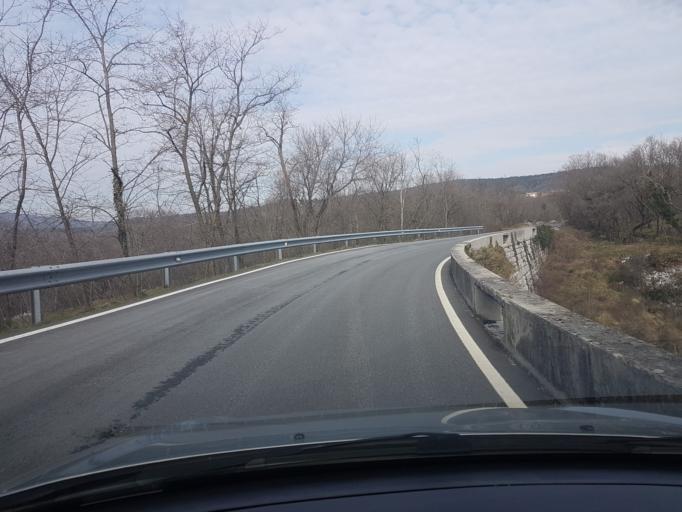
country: IT
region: Friuli Venezia Giulia
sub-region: Provincia di Trieste
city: Aurisina Cave
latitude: 45.7641
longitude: 13.6618
